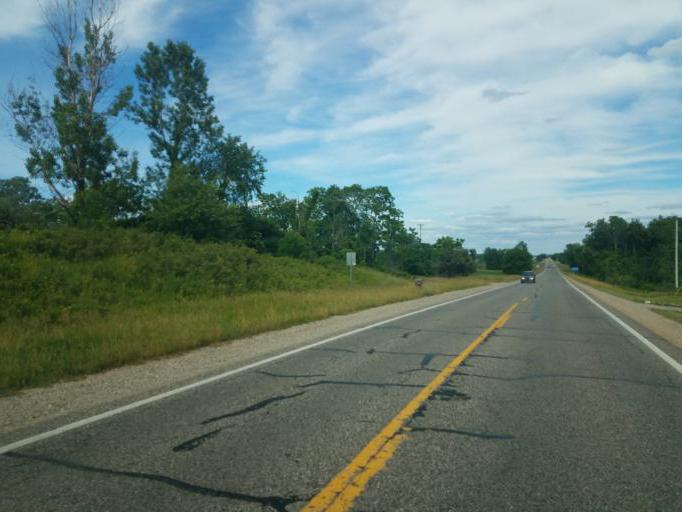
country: US
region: Michigan
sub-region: Eaton County
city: Charlotte
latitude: 42.5679
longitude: -84.9409
